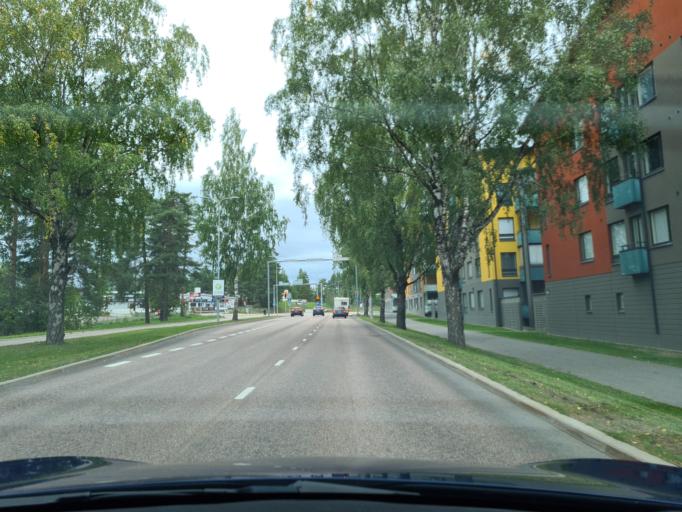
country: FI
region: South Karelia
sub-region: Lappeenranta
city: Lappeenranta
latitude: 61.0469
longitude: 28.1807
